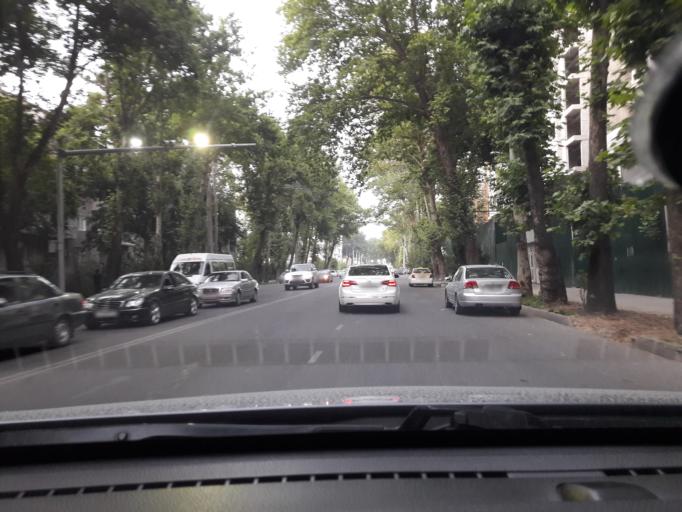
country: TJ
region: Dushanbe
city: Dushanbe
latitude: 38.5690
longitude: 68.7861
